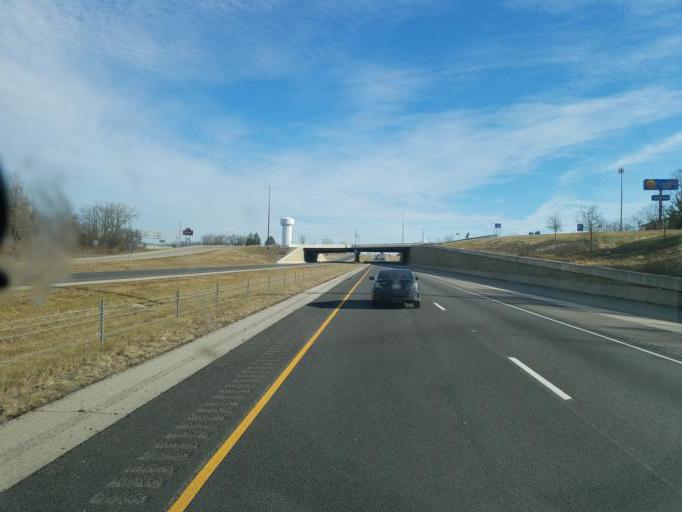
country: US
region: Indiana
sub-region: Wayne County
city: Richmond
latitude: 39.8718
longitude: -84.8917
